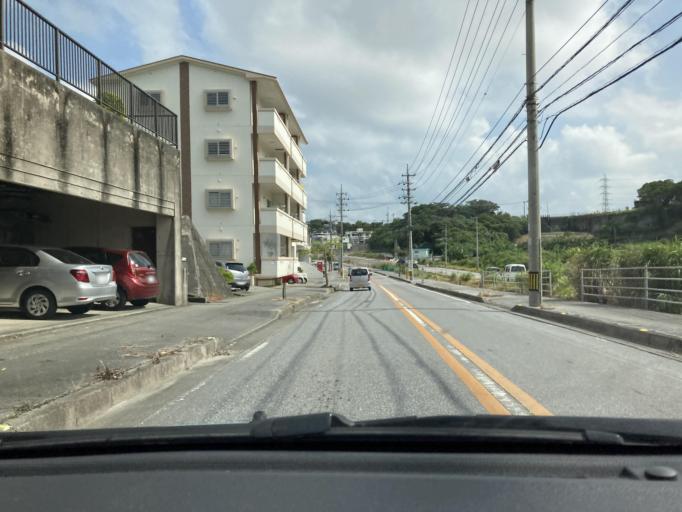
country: JP
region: Okinawa
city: Ginowan
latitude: 26.2403
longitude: 127.7567
